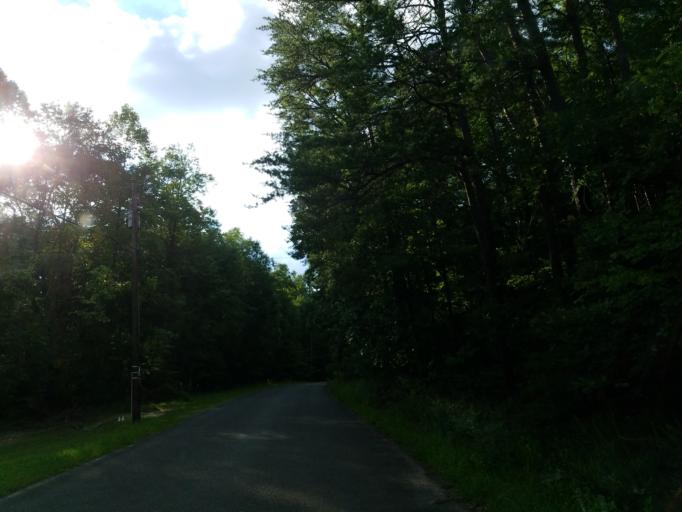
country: US
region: Georgia
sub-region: Gilmer County
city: Ellijay
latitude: 34.6512
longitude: -84.2891
